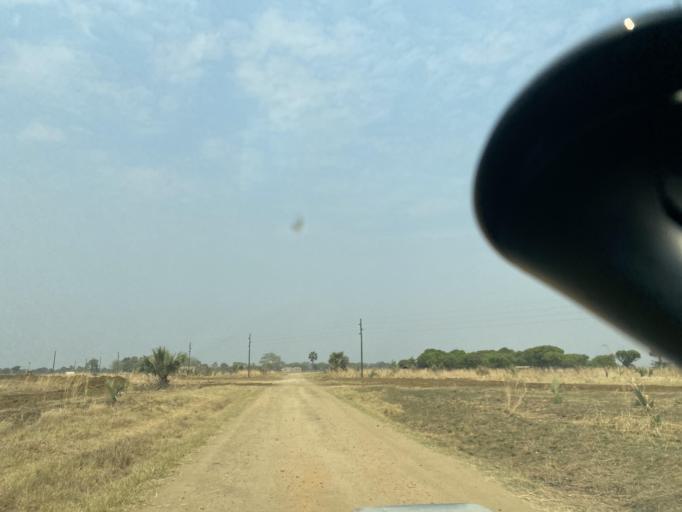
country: ZM
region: Lusaka
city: Kafue
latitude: -15.6517
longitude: 28.0558
